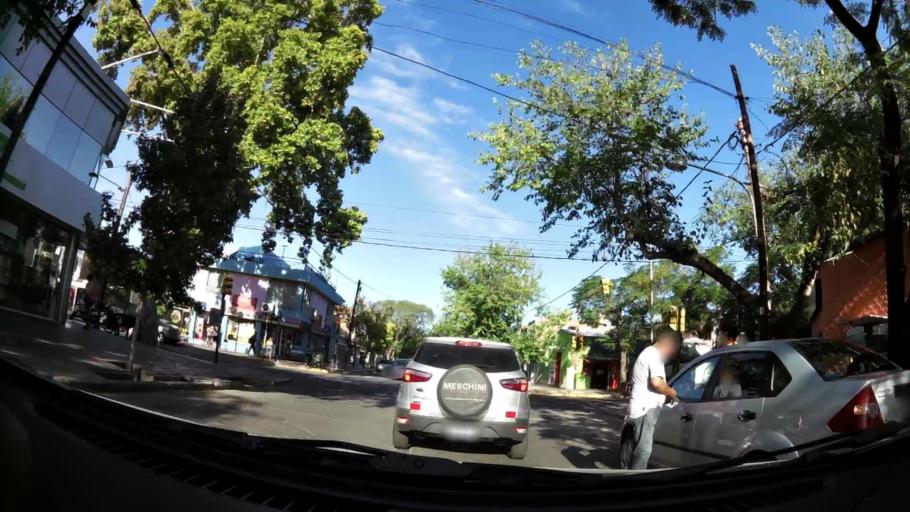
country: AR
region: Mendoza
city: Mendoza
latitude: -32.9040
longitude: -68.8251
